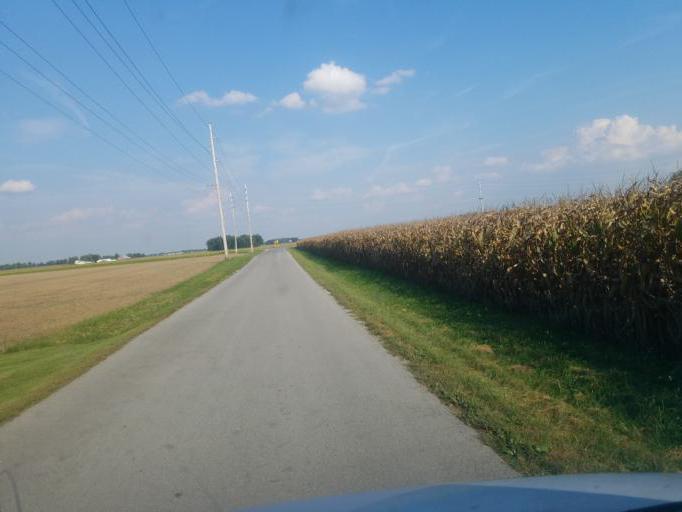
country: US
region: Ohio
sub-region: Wyandot County
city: Carey
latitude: 40.9236
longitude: -83.3066
